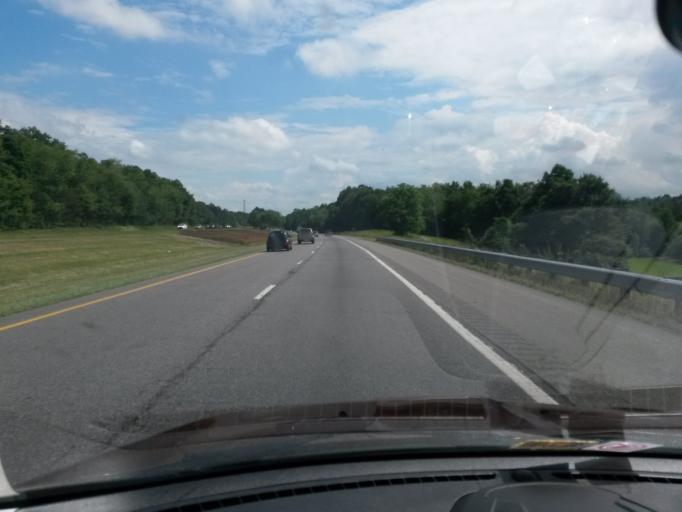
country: US
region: North Carolina
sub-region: Surry County
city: Dobson
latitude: 36.3553
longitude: -80.7985
